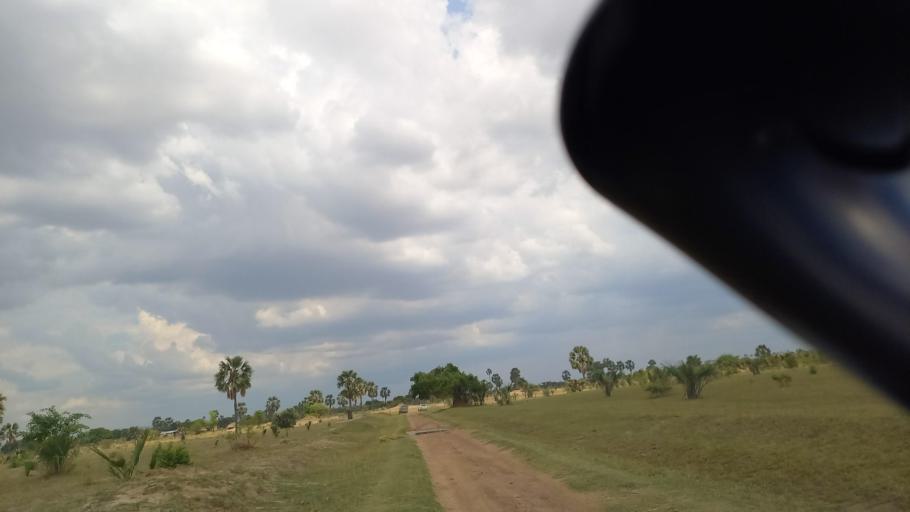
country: ZM
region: Lusaka
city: Kafue
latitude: -15.8271
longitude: 28.0524
